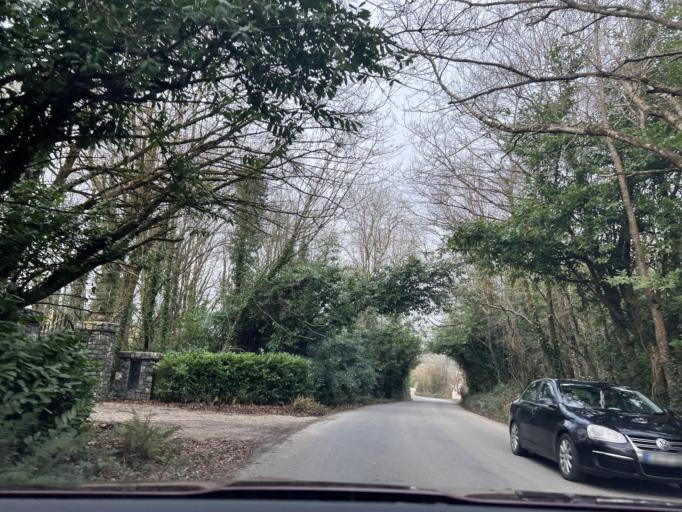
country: IE
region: Leinster
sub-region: Loch Garman
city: Castlebridge
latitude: 52.3817
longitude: -6.5581
